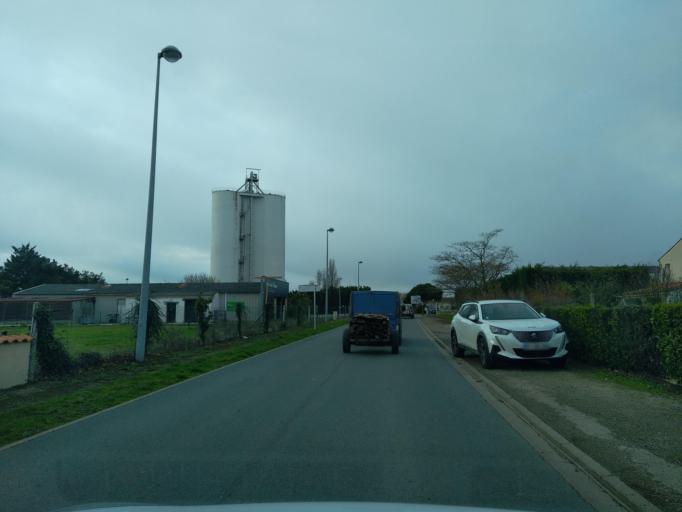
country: FR
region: Pays de la Loire
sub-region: Departement de la Vendee
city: Vix
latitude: 46.3685
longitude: -0.8694
